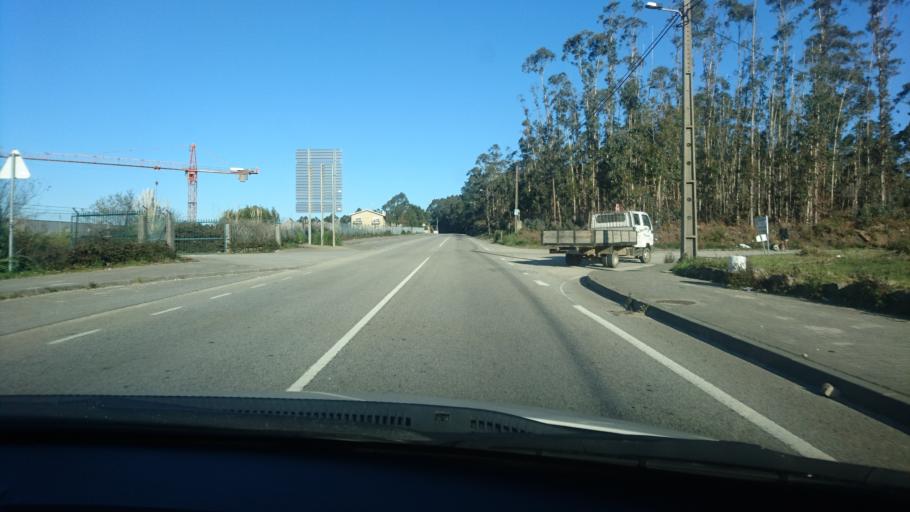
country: PT
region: Aveiro
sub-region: Santa Maria da Feira
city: Arrifana
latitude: 40.9409
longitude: -8.5082
